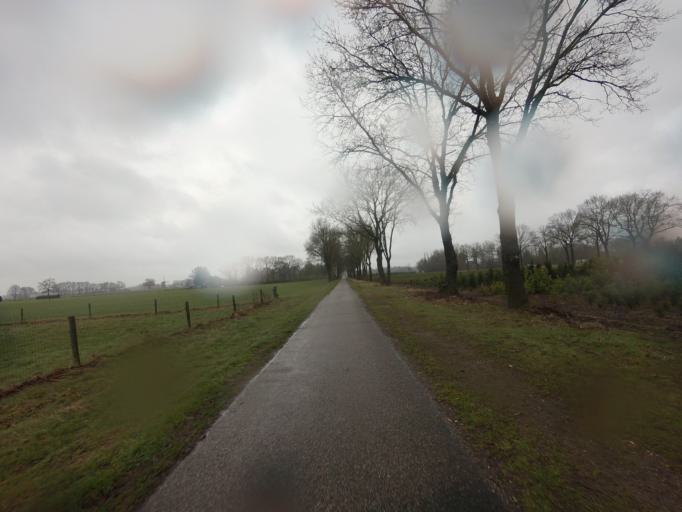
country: NL
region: Gelderland
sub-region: Gemeente Epe
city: Vaassen
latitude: 52.2663
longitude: 5.9686
